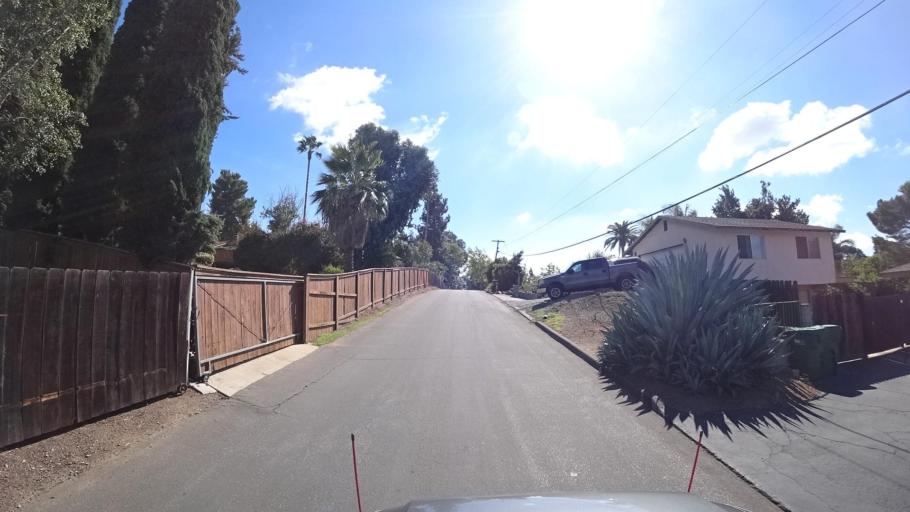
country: US
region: California
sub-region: San Diego County
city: Rancho San Diego
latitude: 32.7694
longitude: -116.9364
